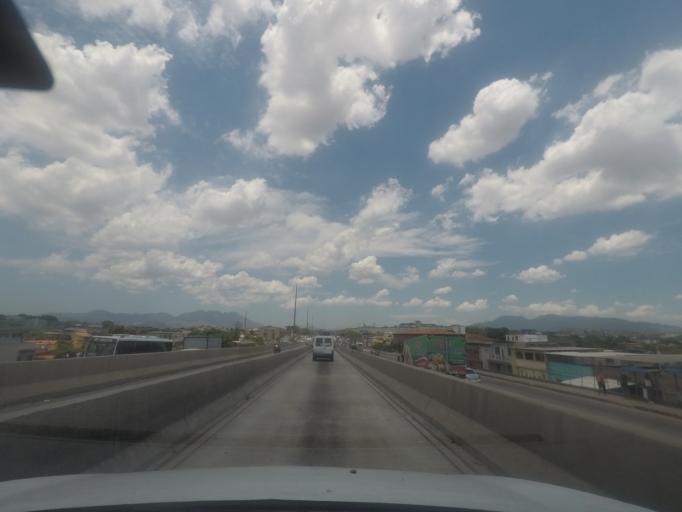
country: BR
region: Rio de Janeiro
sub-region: Sao Joao De Meriti
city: Sao Joao de Meriti
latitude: -22.8294
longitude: -43.3466
